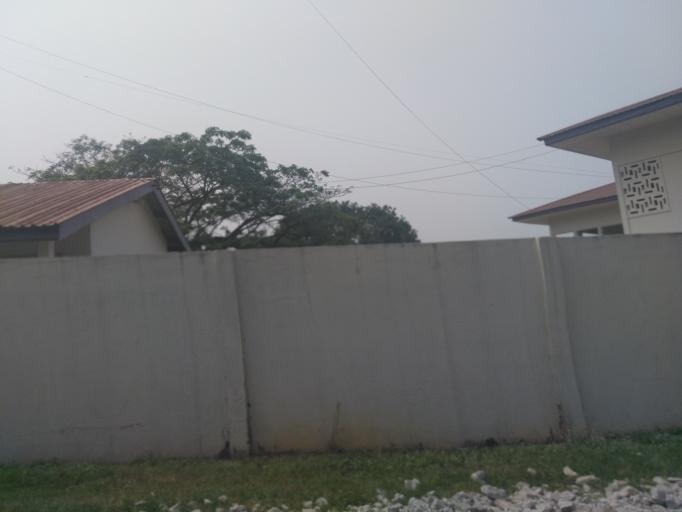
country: GH
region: Ashanti
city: Kumasi
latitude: 6.6760
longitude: -1.6194
